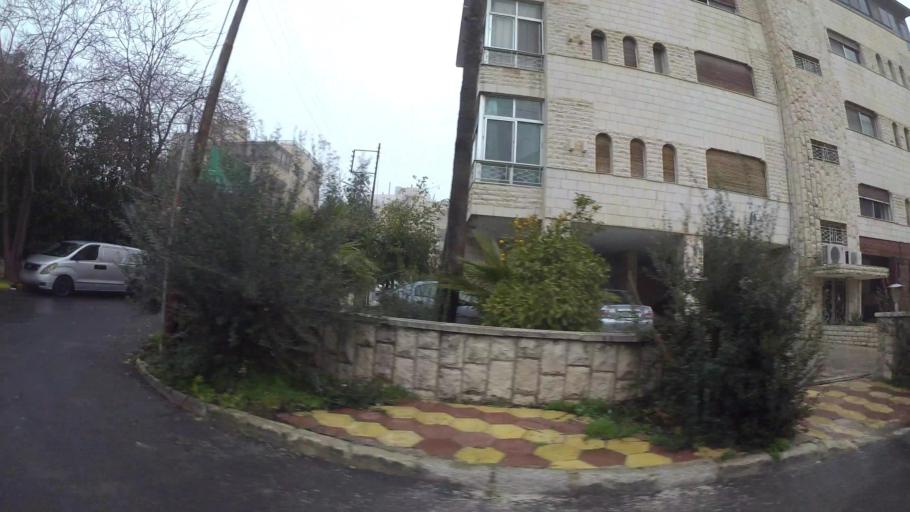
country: JO
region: Amman
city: Wadi as Sir
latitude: 31.9615
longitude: 35.8752
